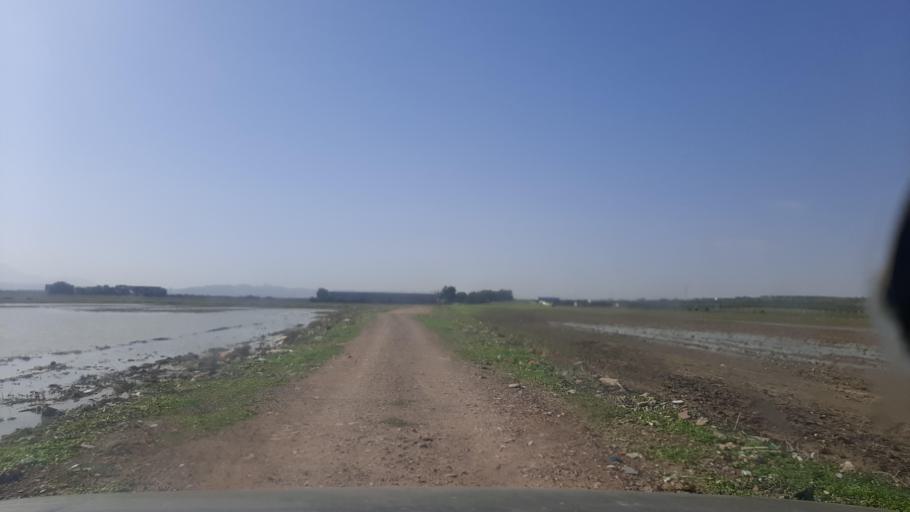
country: TN
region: Tunis
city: La Mohammedia
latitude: 36.6490
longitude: 10.0870
